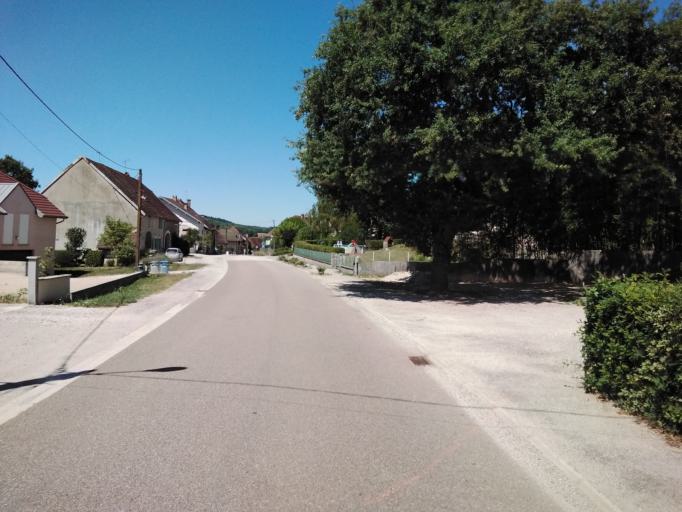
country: FR
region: Franche-Comte
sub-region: Departement du Jura
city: Montmorot
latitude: 46.7568
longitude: 5.5600
